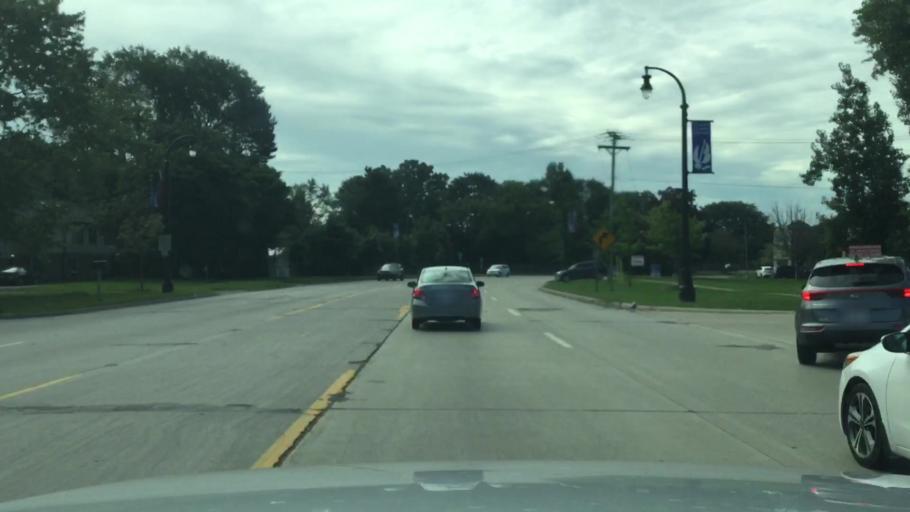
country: US
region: Michigan
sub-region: Wayne County
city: Belleville
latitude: 42.2163
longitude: -83.4853
